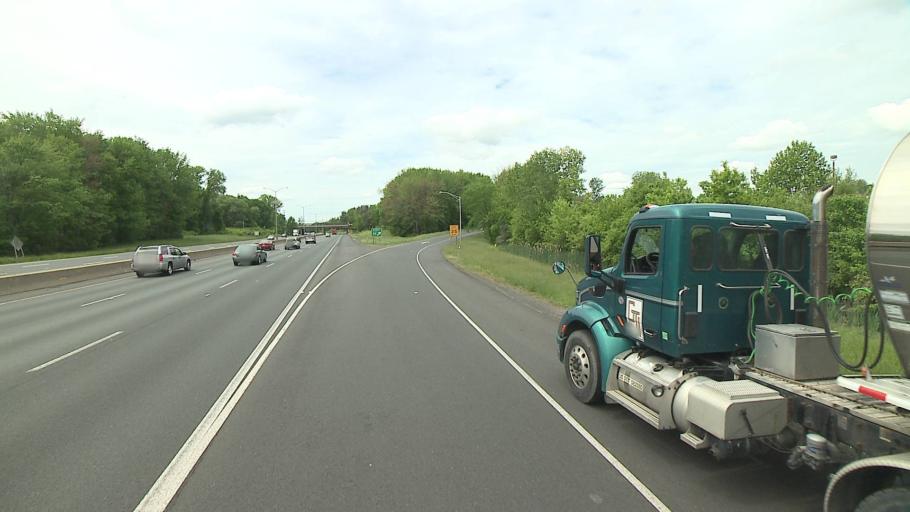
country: US
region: Connecticut
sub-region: Hartford County
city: Enfield
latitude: 41.9551
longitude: -72.5975
